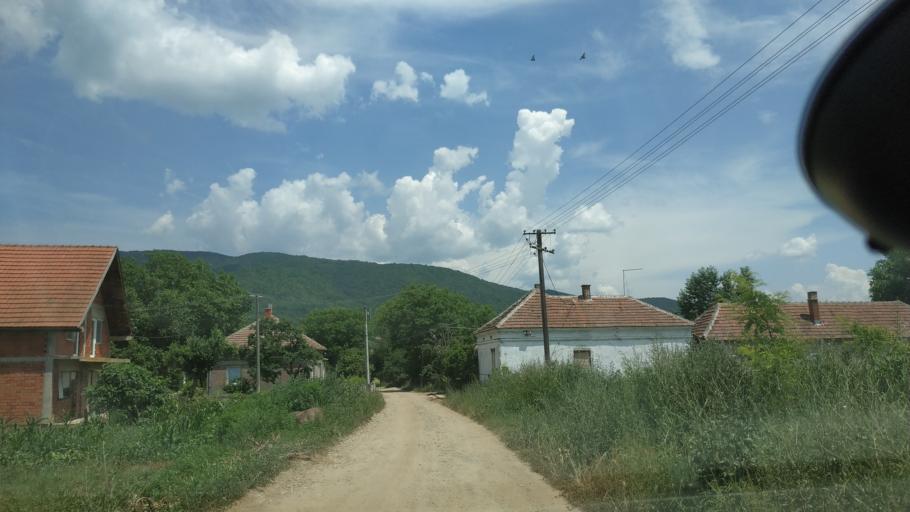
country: RS
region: Central Serbia
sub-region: Nisavski Okrug
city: Aleksinac
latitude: 43.5756
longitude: 21.6949
